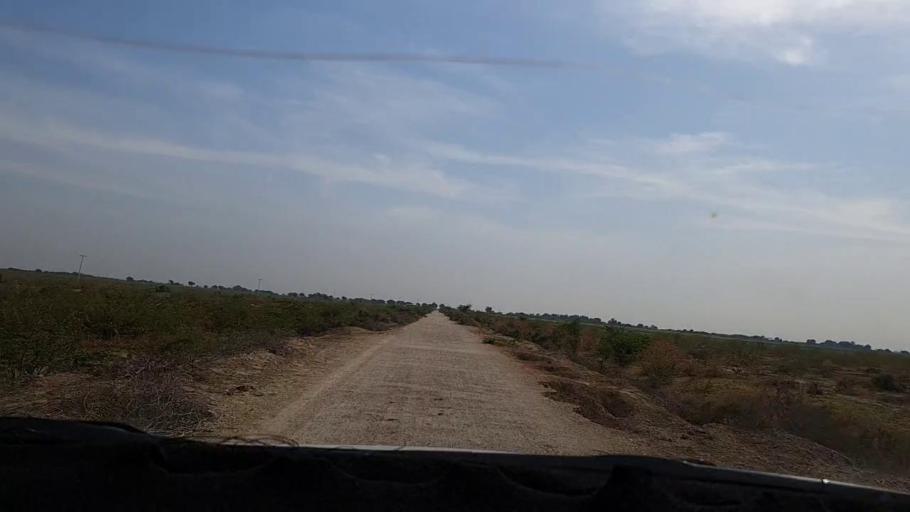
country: PK
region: Sindh
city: Pithoro
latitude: 25.5581
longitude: 69.3309
